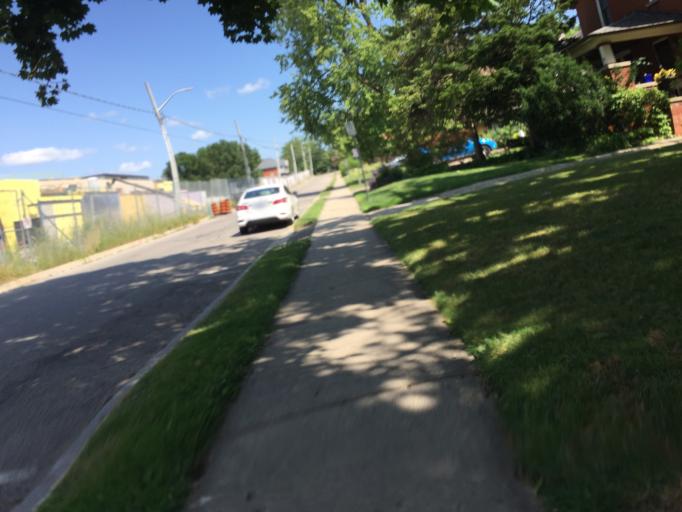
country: CA
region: Ontario
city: Stratford
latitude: 43.3730
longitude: -80.9792
